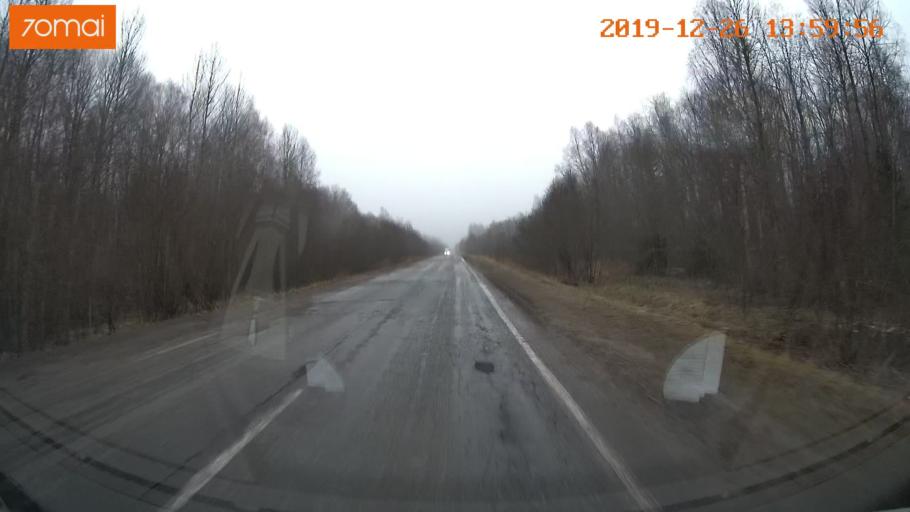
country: RU
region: Jaroslavl
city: Poshekhon'ye
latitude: 58.5617
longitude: 38.7338
